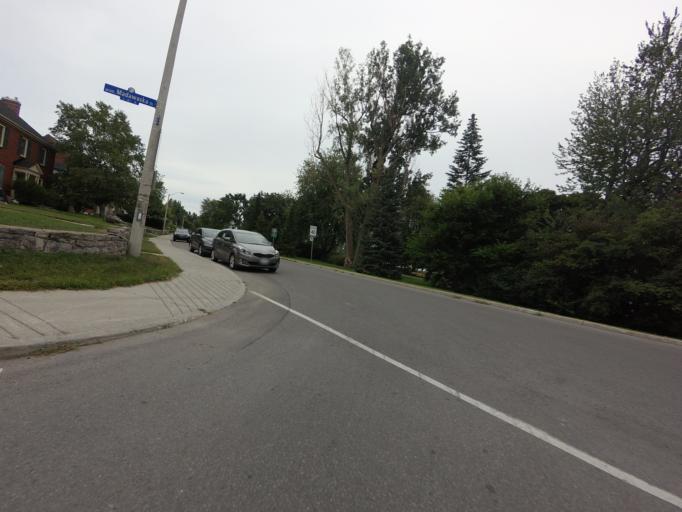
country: CA
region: Ontario
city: Ottawa
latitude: 45.3979
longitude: -75.7012
